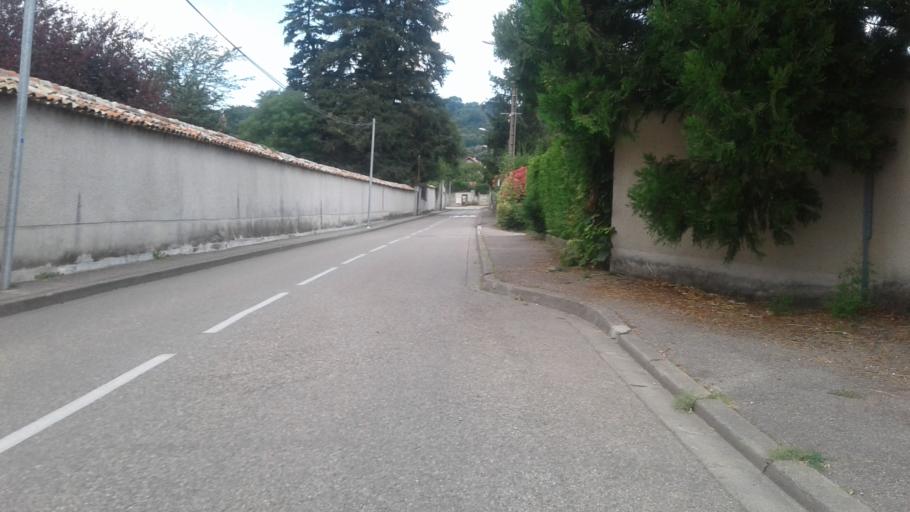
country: FR
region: Rhone-Alpes
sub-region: Departement de l'Ain
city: Beynost
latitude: 45.8371
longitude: 5.0040
